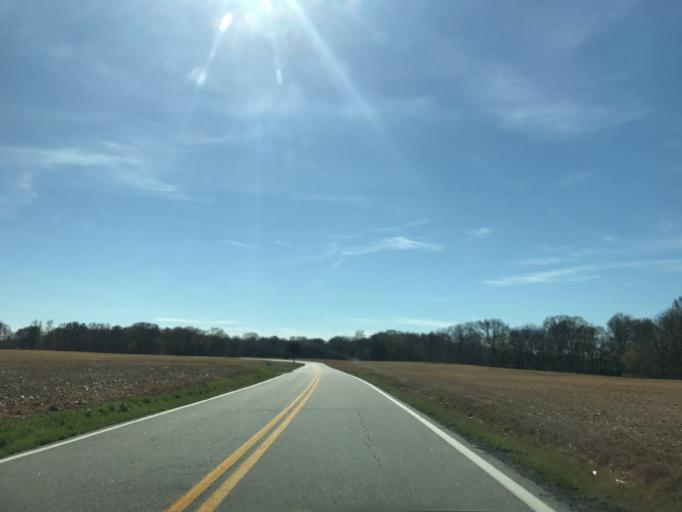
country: US
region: Maryland
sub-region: Caroline County
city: Ridgely
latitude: 38.9759
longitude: -75.9673
